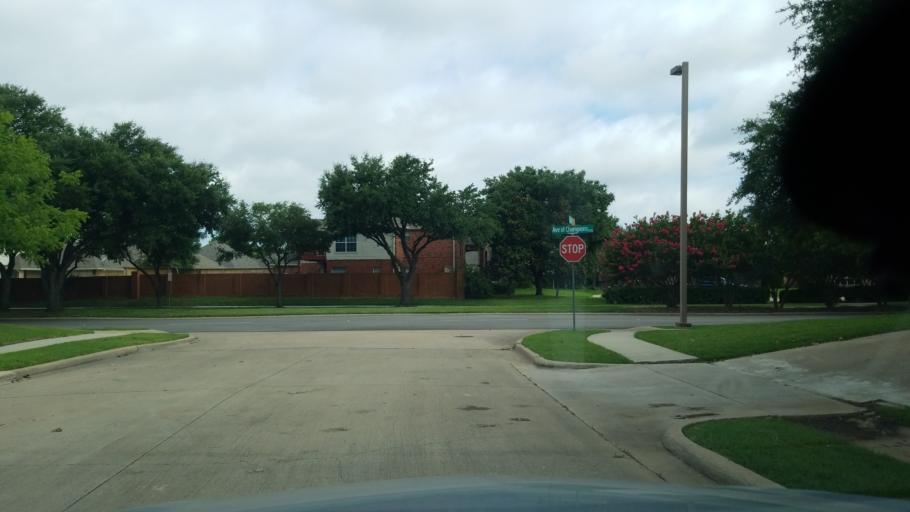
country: US
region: Texas
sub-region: Dallas County
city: Farmers Branch
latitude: 32.9436
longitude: -96.9481
